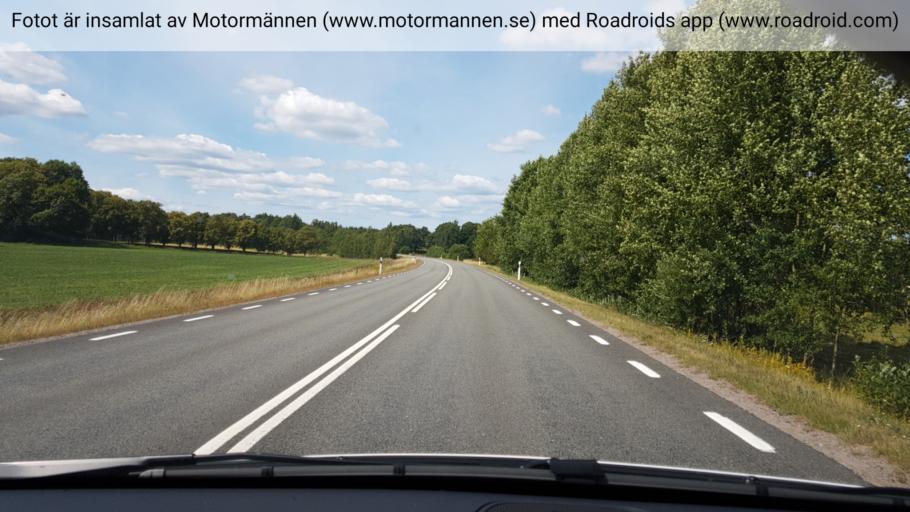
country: SE
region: Vaestra Goetaland
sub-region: Toreboda Kommun
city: Toereboda
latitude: 58.6155
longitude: 13.9937
